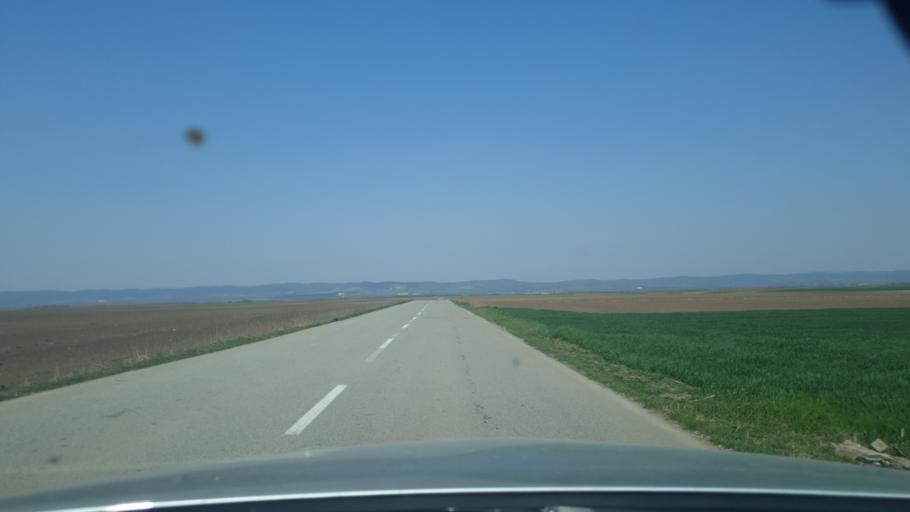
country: RS
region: Autonomna Pokrajina Vojvodina
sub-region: Sremski Okrug
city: Ruma
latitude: 45.0282
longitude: 19.7625
